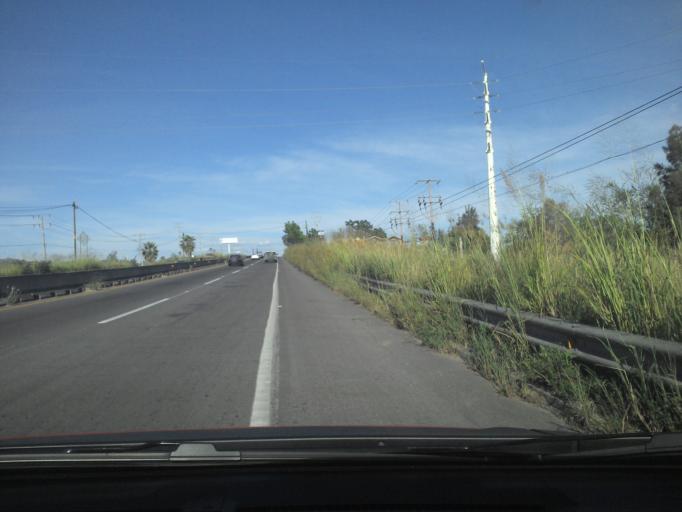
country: MX
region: Jalisco
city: Tala
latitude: 20.6710
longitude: -103.7125
